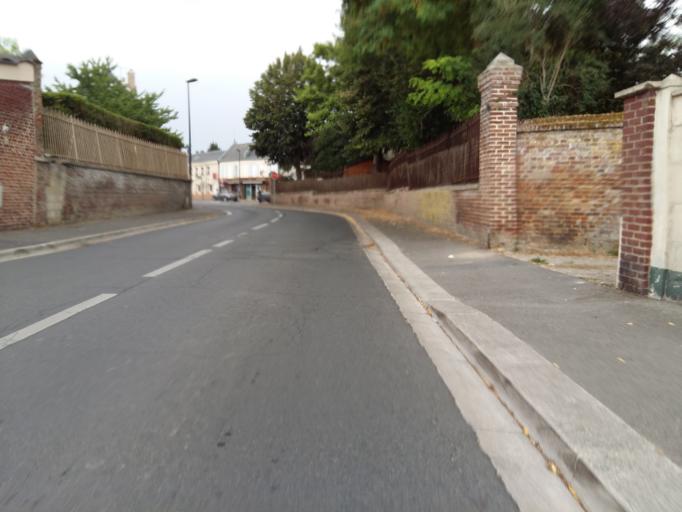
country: FR
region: Picardie
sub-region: Departement de la Somme
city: Camon
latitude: 49.8868
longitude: 2.3429
